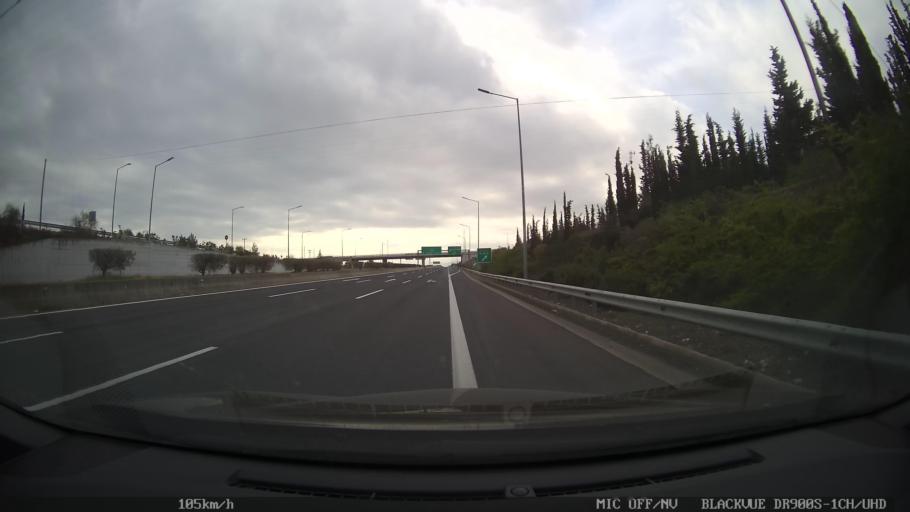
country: GR
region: Central Macedonia
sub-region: Nomos Pierias
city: Litochoro
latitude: 40.1347
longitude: 22.5452
